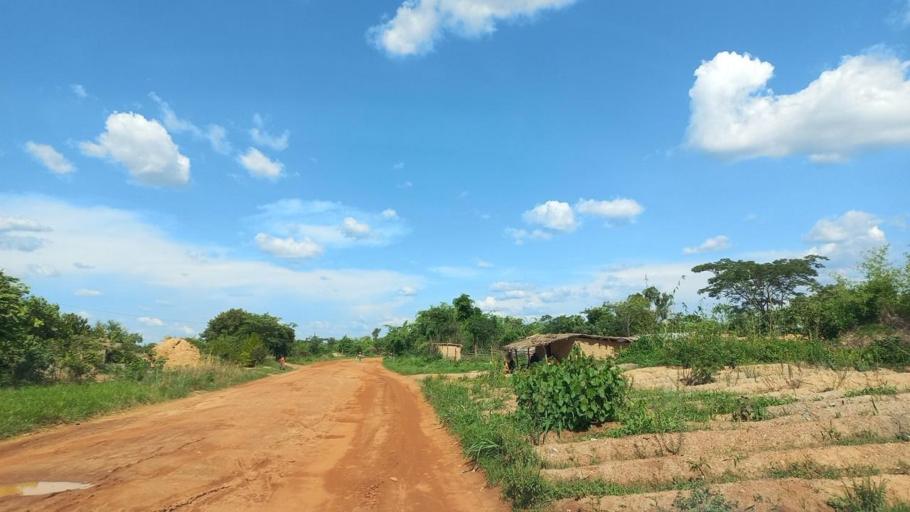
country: ZM
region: Copperbelt
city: Kitwe
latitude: -12.8655
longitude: 28.3721
